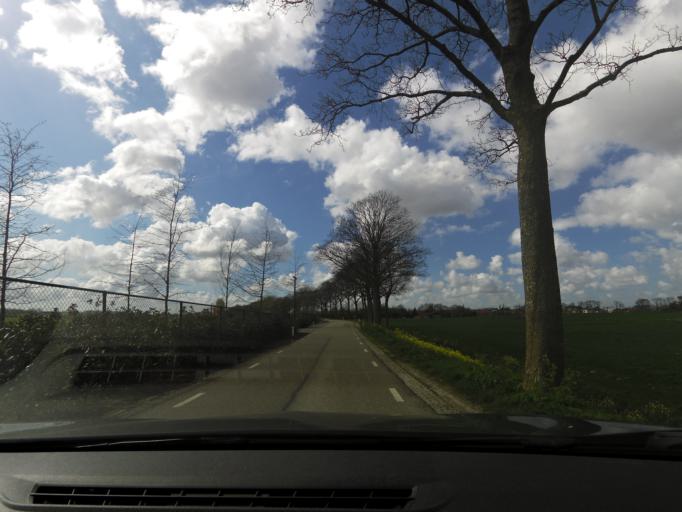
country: NL
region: South Holland
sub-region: Gemeente Albrandswaard
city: Rhoon
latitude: 51.8504
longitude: 4.4442
